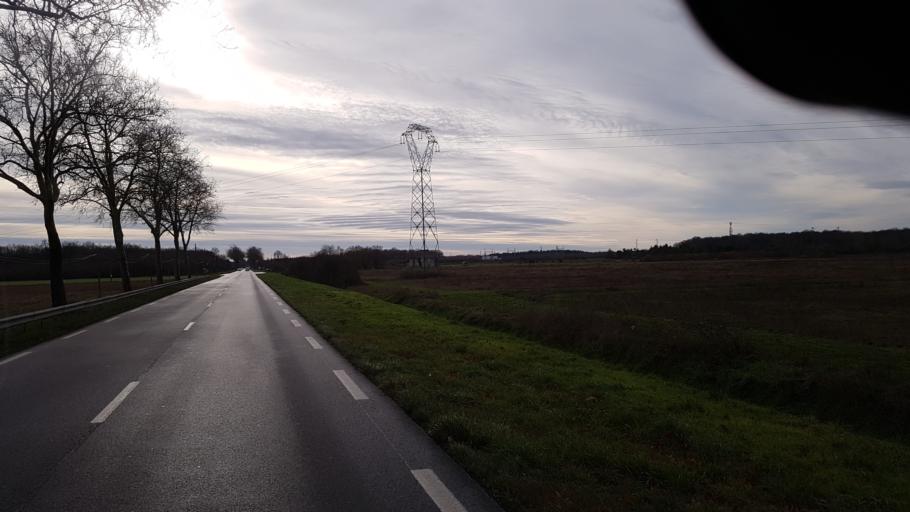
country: FR
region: Centre
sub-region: Departement du Loiret
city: Saint-Cyr-en-Val
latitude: 47.8008
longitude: 1.9311
